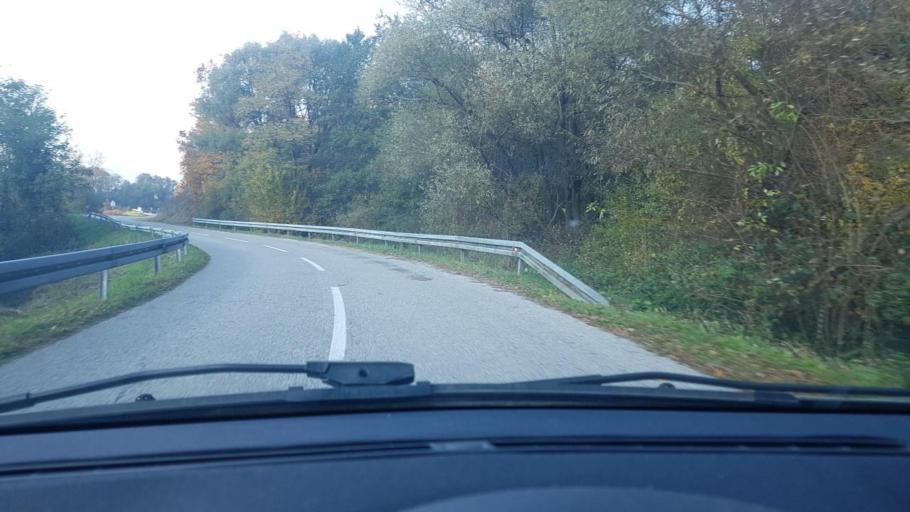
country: SI
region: Rogaska Slatina
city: Rogaska Slatina
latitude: 46.1987
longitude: 15.6480
